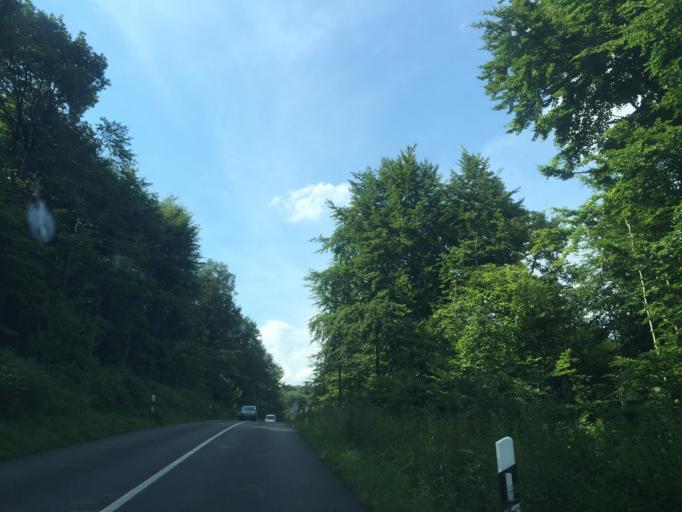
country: DE
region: Baden-Wuerttemberg
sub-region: Karlsruhe Region
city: Gaiberg
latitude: 49.3777
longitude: 8.7256
